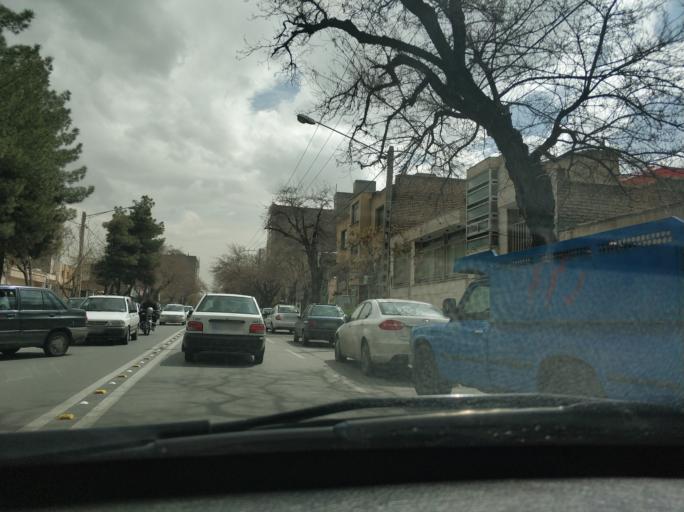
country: IR
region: Razavi Khorasan
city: Mashhad
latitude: 36.2817
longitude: 59.5729
